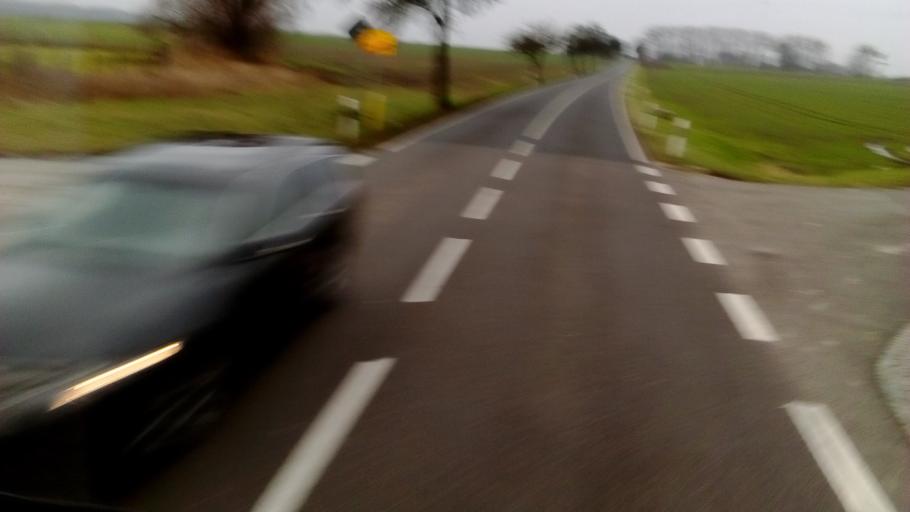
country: DE
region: Mecklenburg-Vorpommern
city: Viereck
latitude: 53.4921
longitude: 14.0914
